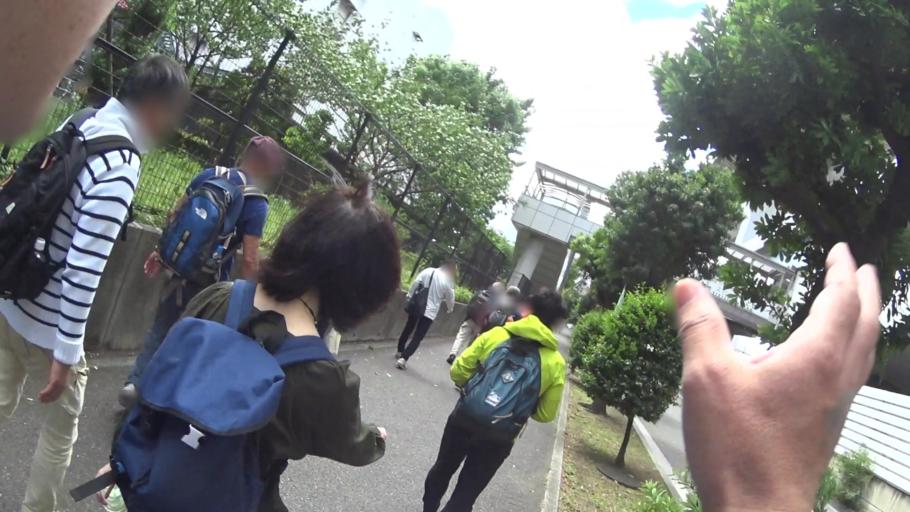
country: JP
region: Tokyo
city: Tokyo
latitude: 35.6409
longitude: 139.7603
